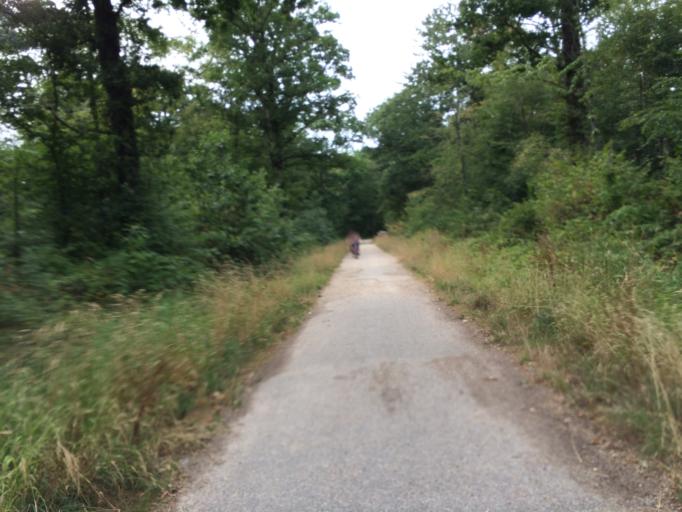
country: FR
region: Ile-de-France
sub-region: Departement de l'Essonne
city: Quincy-sous-Senart
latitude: 48.6599
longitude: 2.5420
